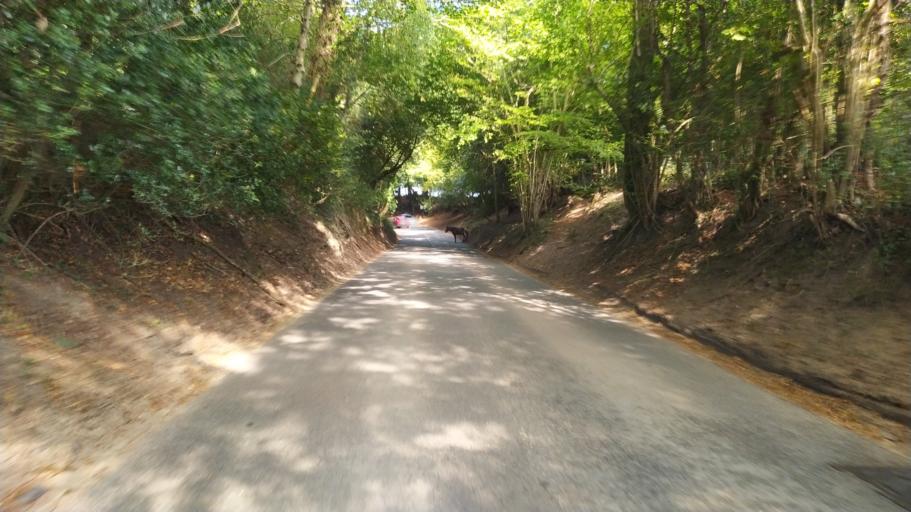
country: GB
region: England
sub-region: Hampshire
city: Bransgore
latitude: 50.8287
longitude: -1.7070
